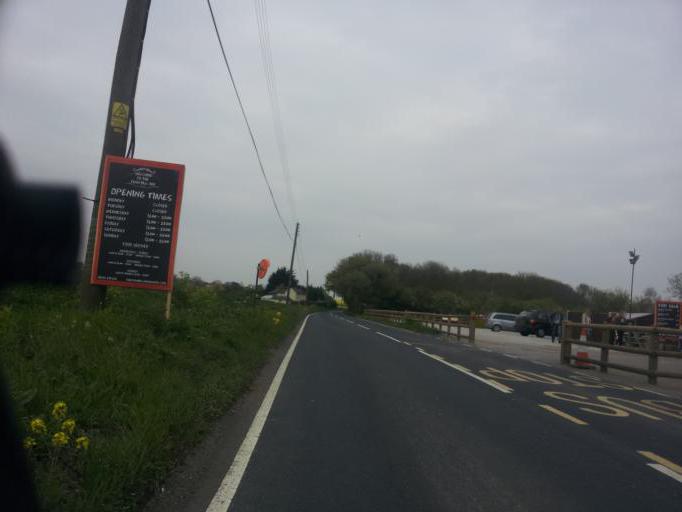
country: GB
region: England
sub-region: Medway
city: High Halstow
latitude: 51.4518
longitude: 0.5889
